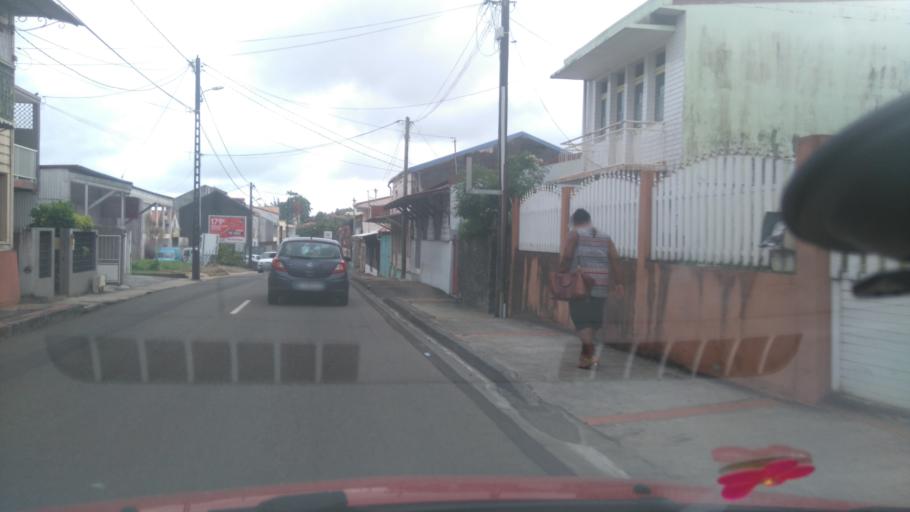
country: MQ
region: Martinique
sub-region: Martinique
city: Saint-Esprit
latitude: 14.5612
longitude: -60.9382
